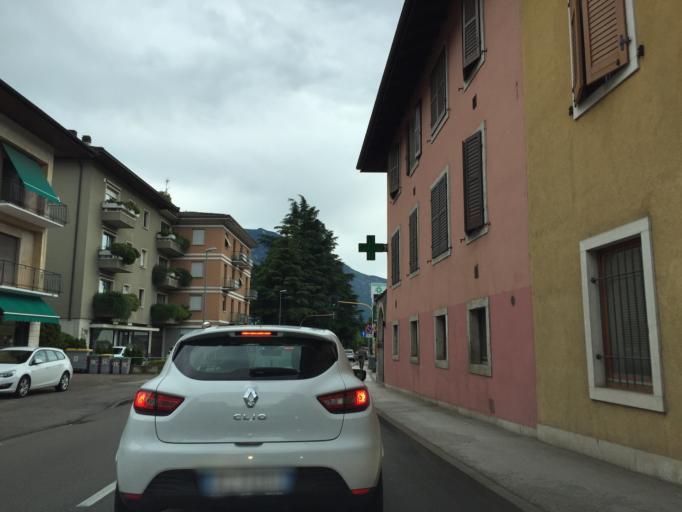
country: IT
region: Trentino-Alto Adige
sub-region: Provincia di Trento
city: Trento
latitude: 46.0539
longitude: 11.1297
